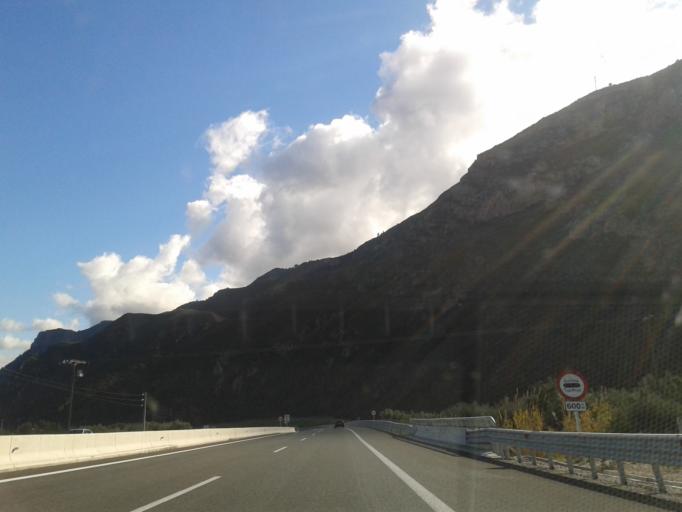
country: GR
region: West Greece
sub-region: Nomos Achaias
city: Temeni
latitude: 38.1939
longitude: 22.1547
